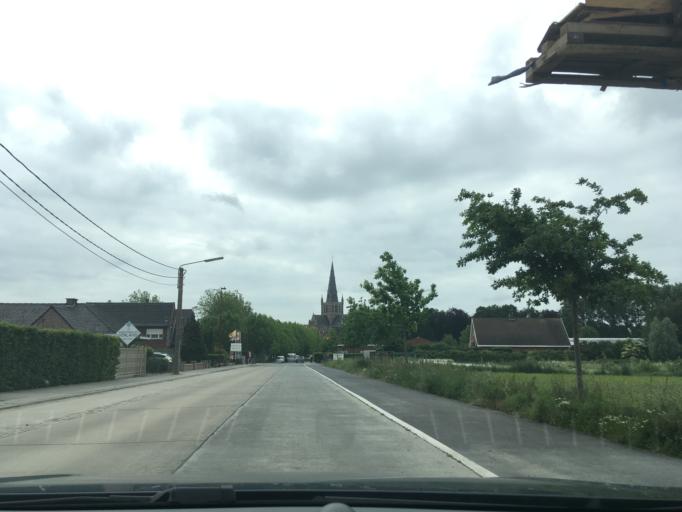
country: BE
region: Flanders
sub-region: Provincie West-Vlaanderen
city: Ledegem
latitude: 50.8545
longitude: 3.0919
